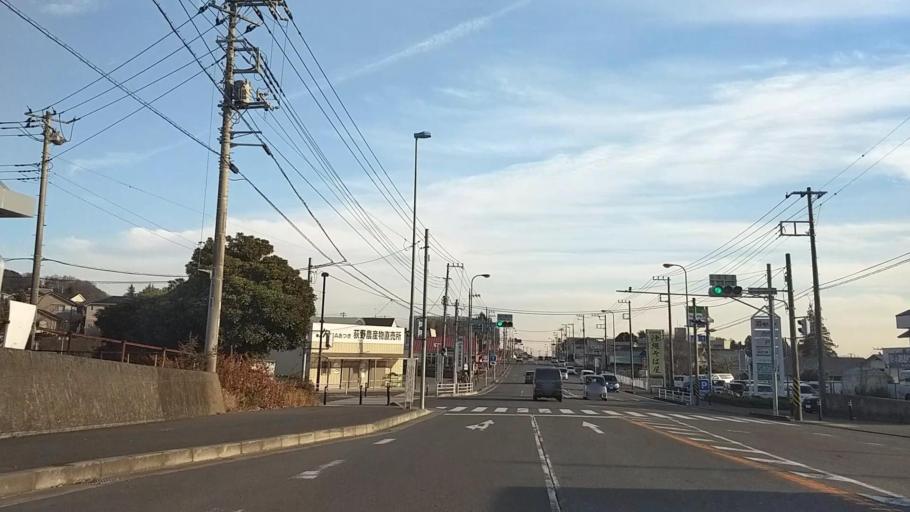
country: JP
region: Kanagawa
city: Atsugi
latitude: 35.4940
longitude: 139.3181
